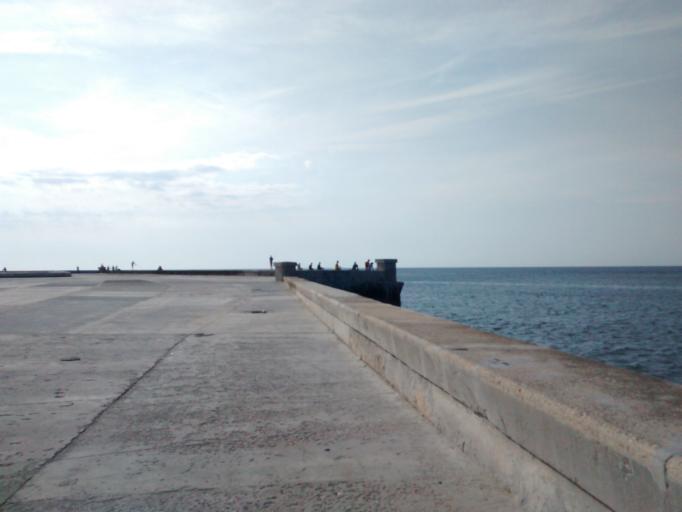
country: CU
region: La Habana
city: Centro Habana
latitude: 23.1465
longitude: -82.3568
